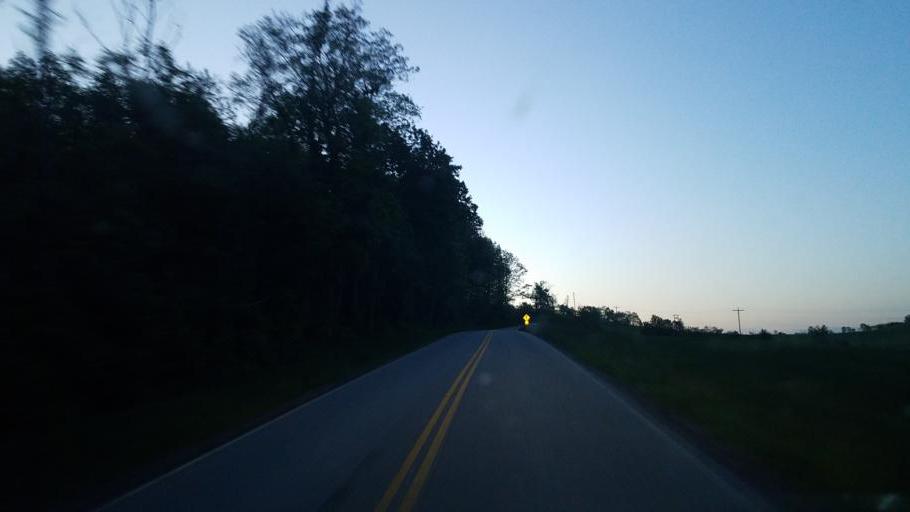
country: US
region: Ohio
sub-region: Belmont County
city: Barnesville
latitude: 40.0923
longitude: -81.3275
